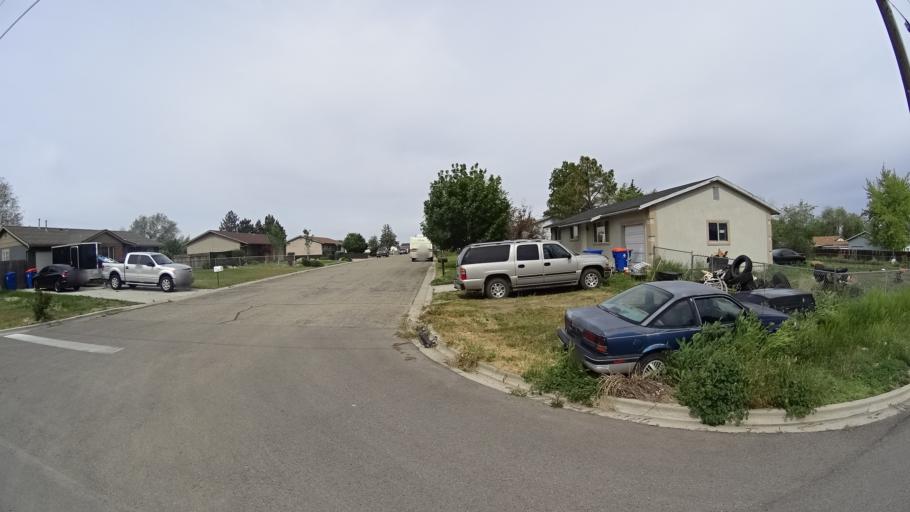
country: US
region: Idaho
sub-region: Ada County
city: Meridian
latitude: 43.5312
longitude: -116.3146
